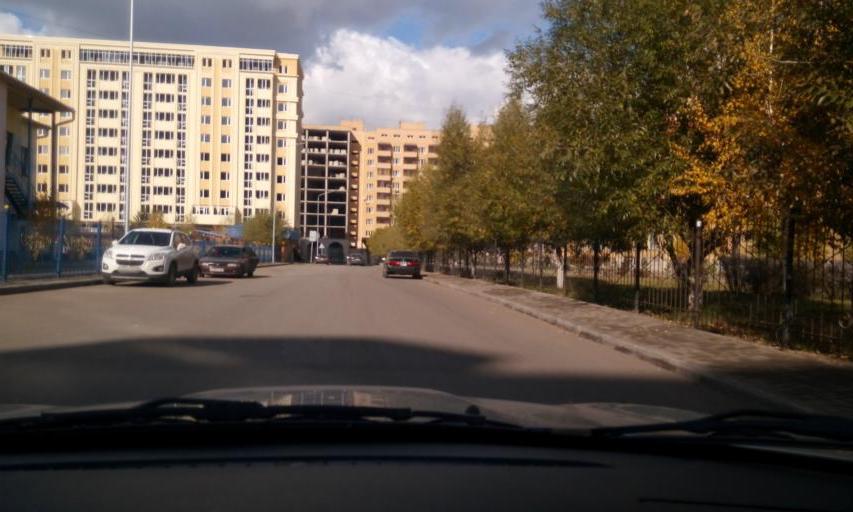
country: KZ
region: Astana Qalasy
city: Astana
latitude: 51.1702
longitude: 71.4010
